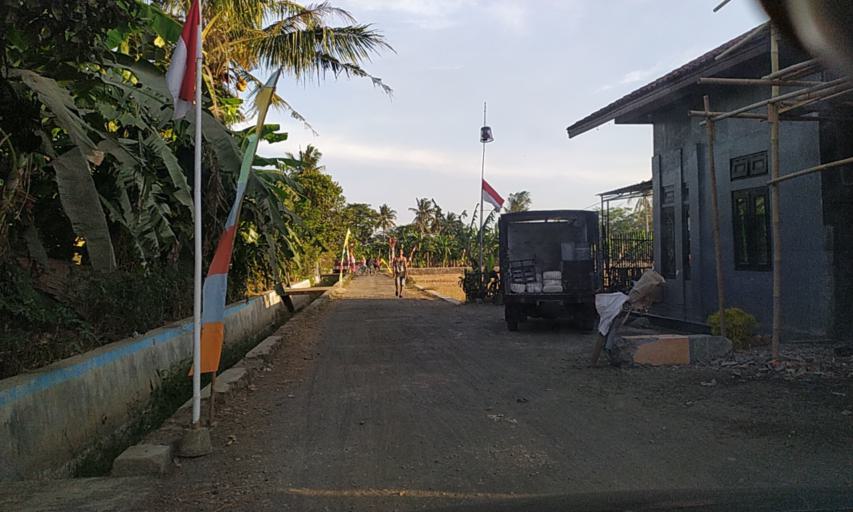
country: ID
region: Central Java
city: Rejanegara
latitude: -7.6936
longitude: 109.0443
